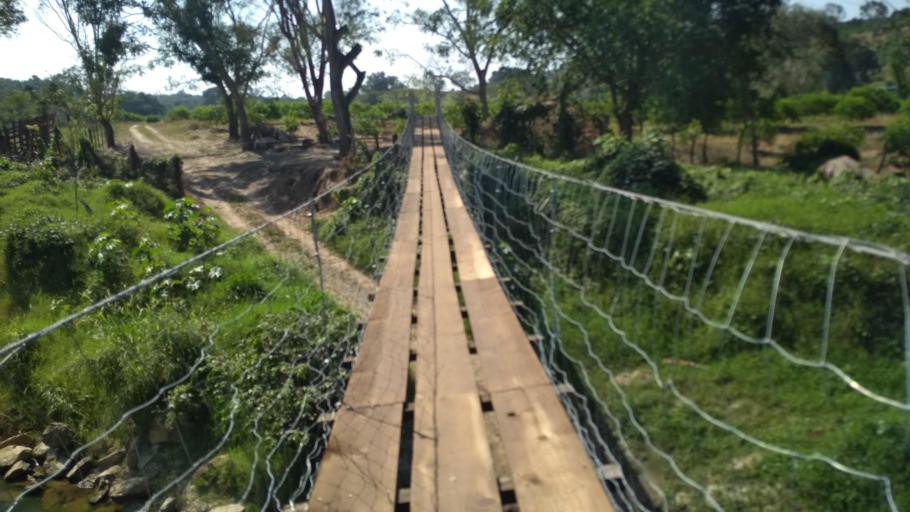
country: MX
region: Puebla
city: San Jose Acateno
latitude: 20.1566
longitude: -97.1791
